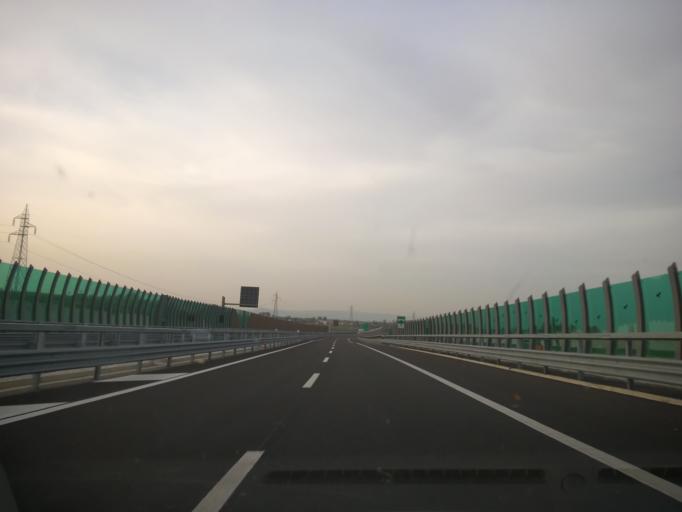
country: IT
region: Veneto
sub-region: Provincia di Padova
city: Saletto
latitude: 45.2258
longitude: 11.5514
